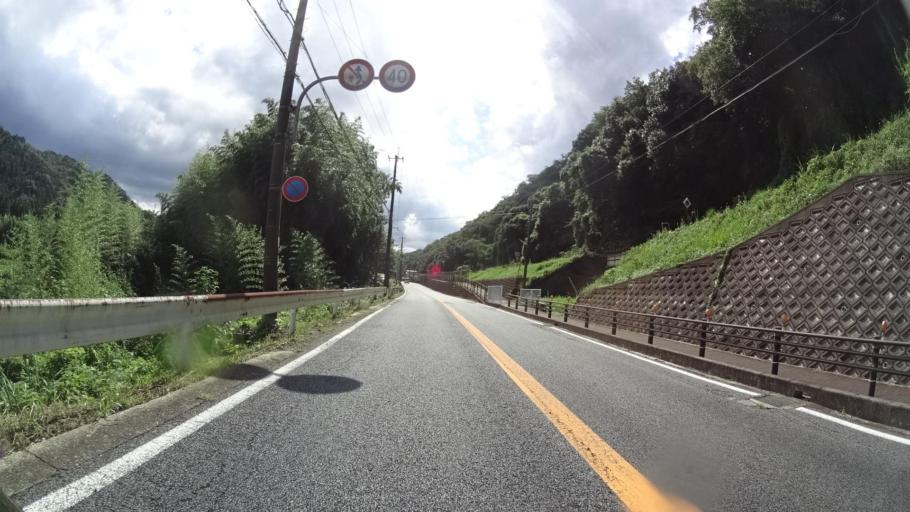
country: JP
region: Mie
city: Ueno-ebisumachi
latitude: 34.7732
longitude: 135.9904
